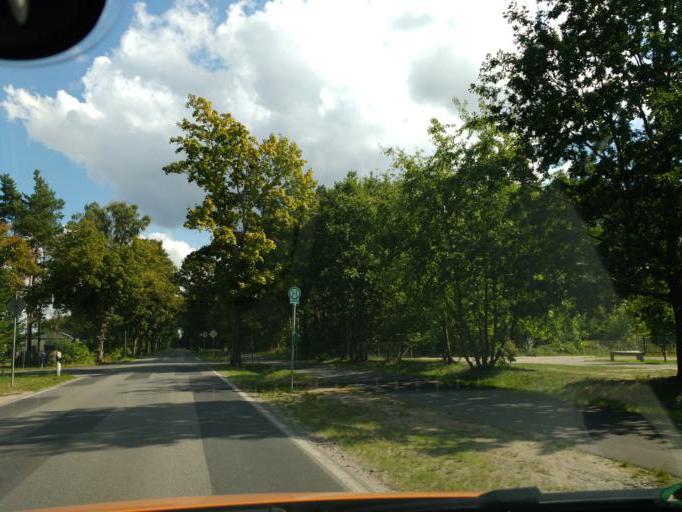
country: DE
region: Brandenburg
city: Wandlitz
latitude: 52.7446
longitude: 13.4131
